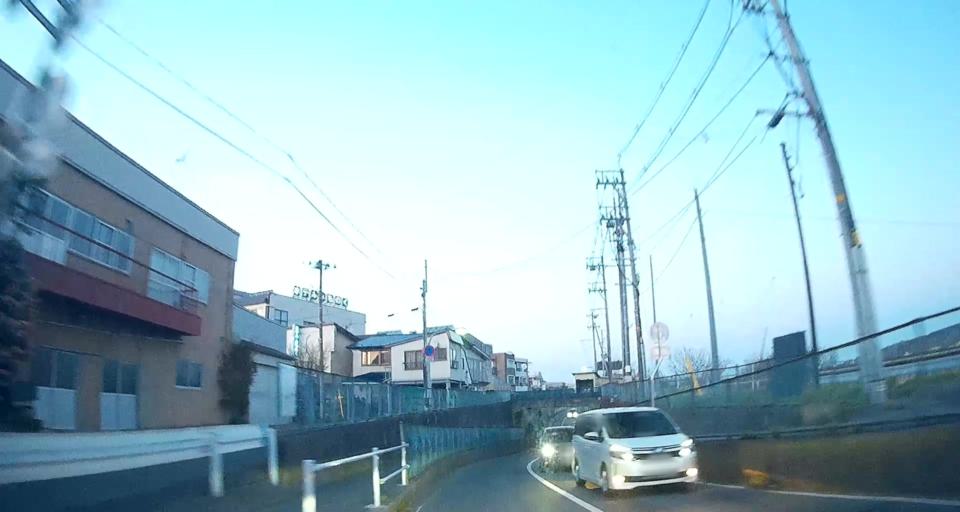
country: JP
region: Aomori
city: Hachinohe
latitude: 40.1879
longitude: 141.7708
